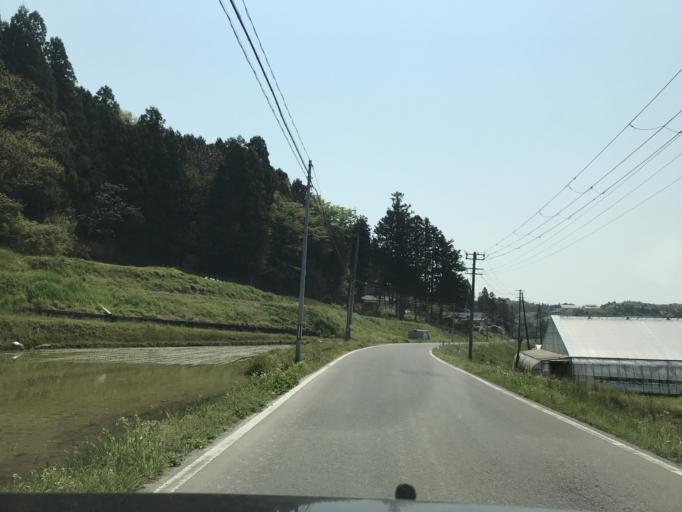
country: JP
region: Iwate
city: Ichinoseki
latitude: 38.8367
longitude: 141.0775
